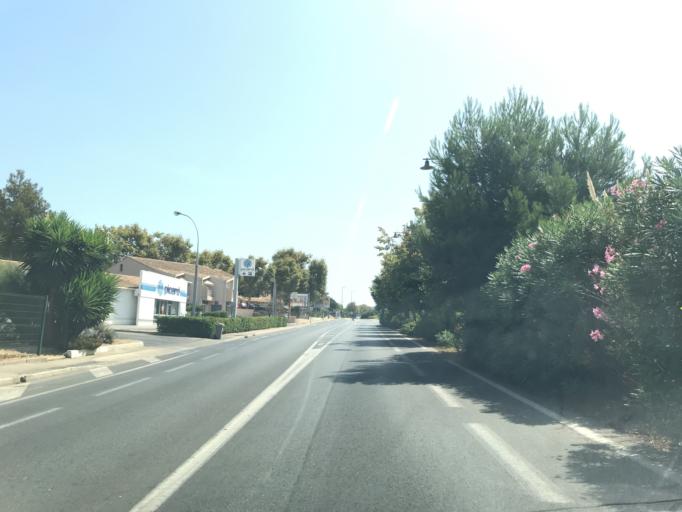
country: FR
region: Provence-Alpes-Cote d'Azur
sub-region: Departement du Var
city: Six-Fours-les-Plages
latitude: 43.0999
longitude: 5.8252
